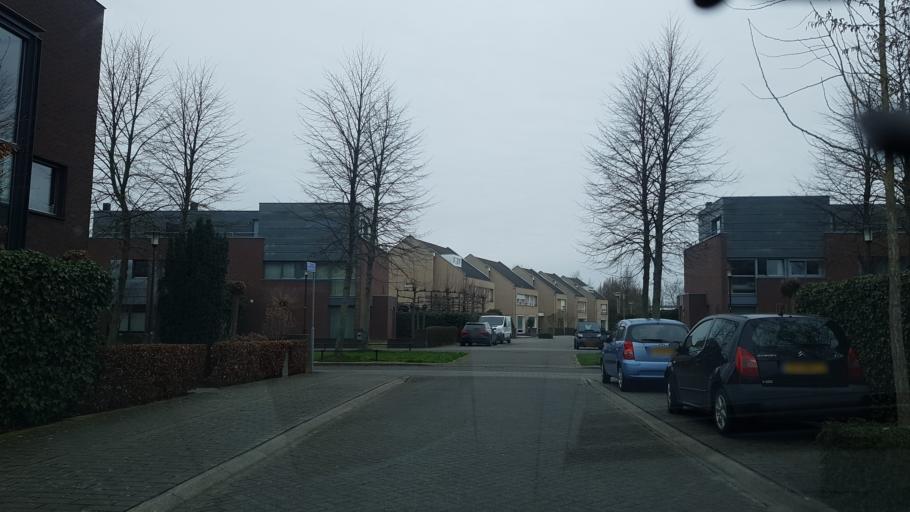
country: NL
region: Limburg
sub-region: Gemeente Maastricht
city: Heer
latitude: 50.8515
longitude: 5.7259
